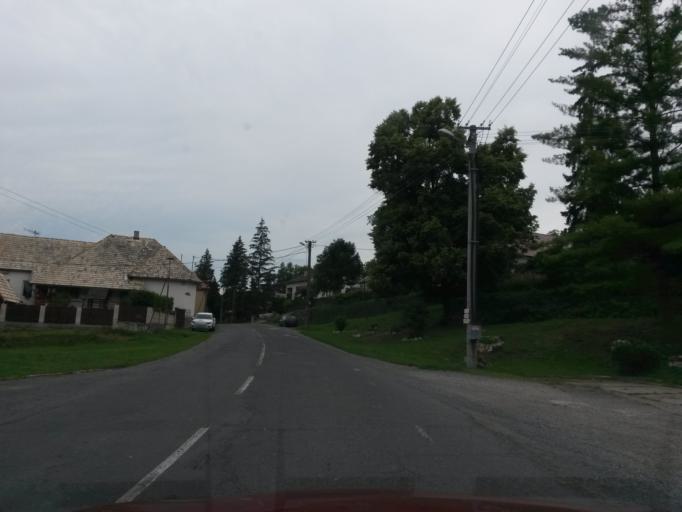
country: SK
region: Banskobystricky
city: Velky Krtis
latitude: 48.3117
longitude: 19.3966
